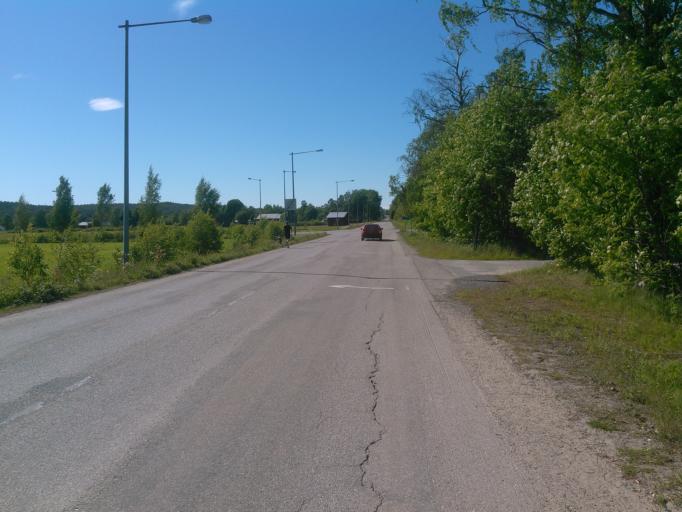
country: SE
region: Vaesterbotten
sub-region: Umea Kommun
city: Roback
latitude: 63.8200
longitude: 20.1975
